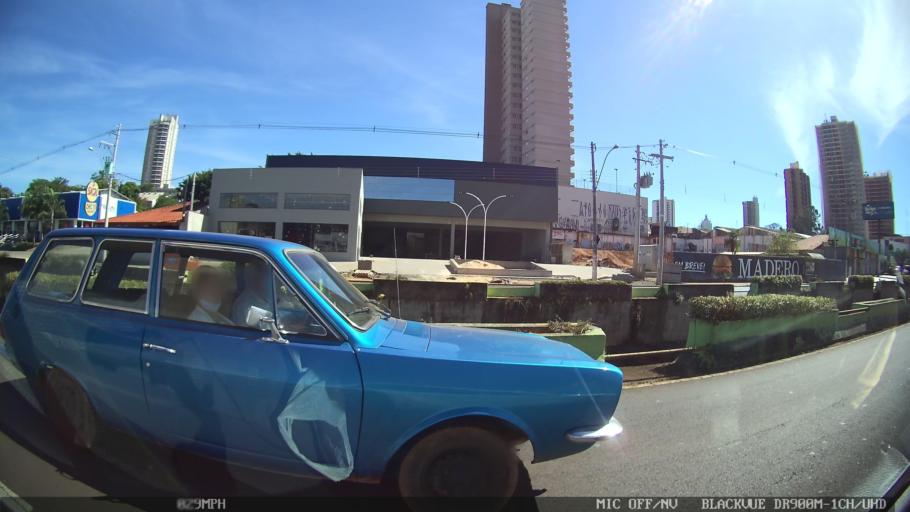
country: BR
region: Sao Paulo
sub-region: Franca
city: Franca
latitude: -20.5417
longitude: -47.3955
